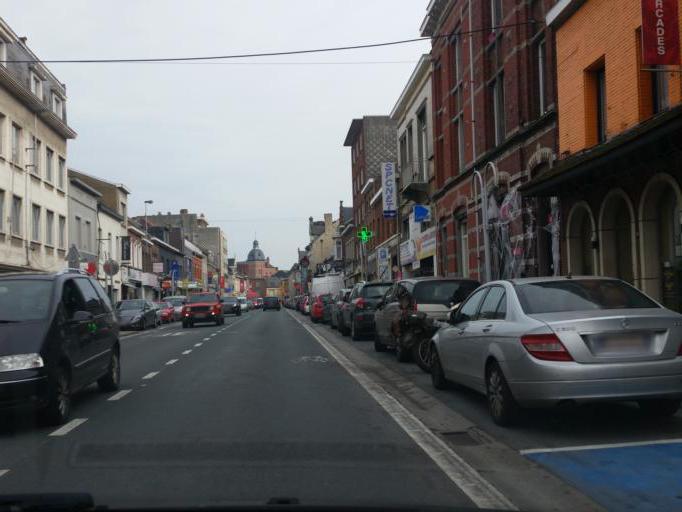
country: BE
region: Wallonia
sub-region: Province du Brabant Wallon
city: Tubize
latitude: 50.6910
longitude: 4.2031
